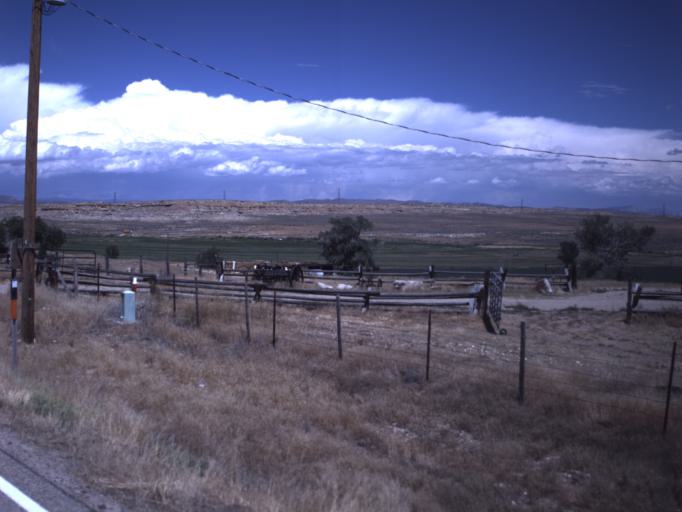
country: US
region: Utah
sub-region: Uintah County
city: Maeser
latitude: 40.2447
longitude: -109.6843
